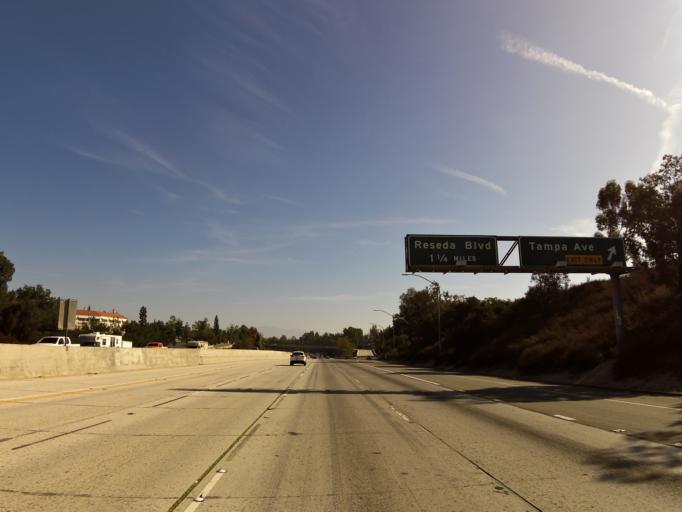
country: US
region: California
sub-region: Los Angeles County
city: Chatsworth
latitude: 34.2727
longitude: -118.5604
